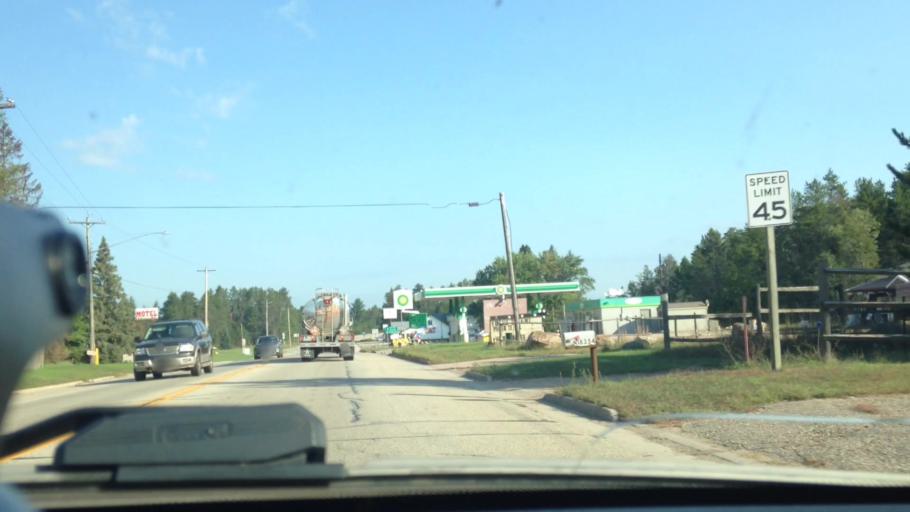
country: US
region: Wisconsin
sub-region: Marinette County
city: Niagara
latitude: 45.6211
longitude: -87.9951
